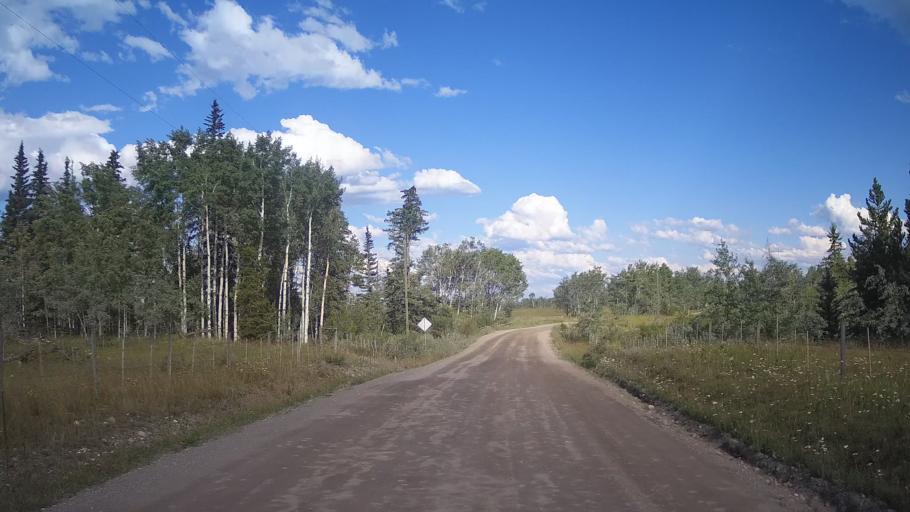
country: CA
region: British Columbia
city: Cache Creek
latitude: 51.2581
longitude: -121.6846
